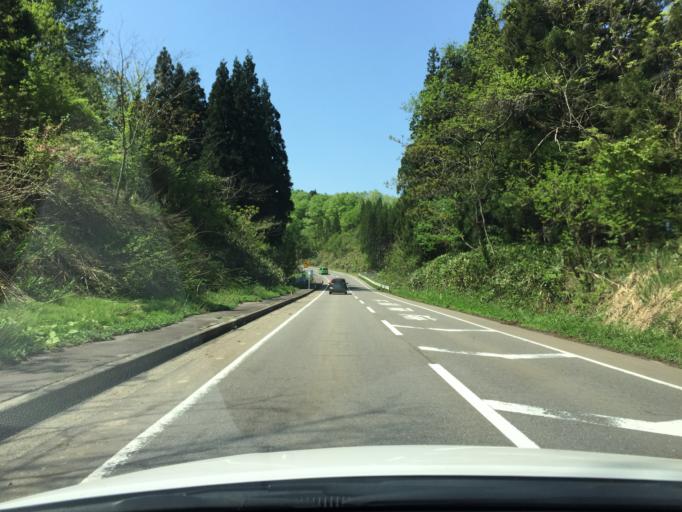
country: JP
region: Niigata
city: Kamo
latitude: 37.5865
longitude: 139.0931
